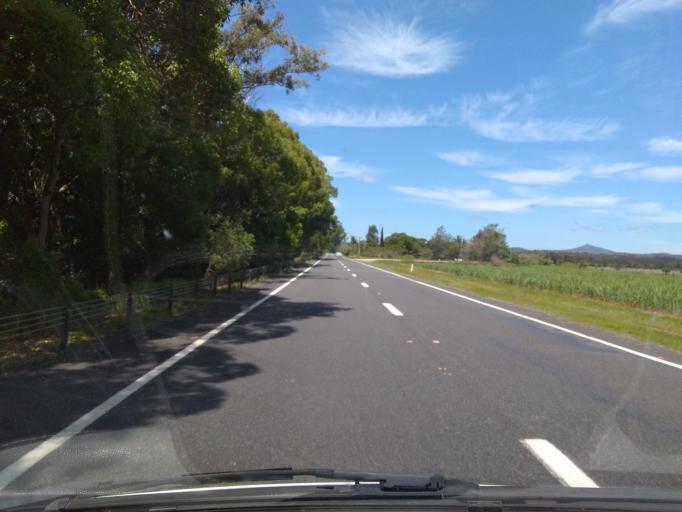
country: AU
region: New South Wales
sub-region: Clarence Valley
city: Maclean
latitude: -29.5418
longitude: 153.1697
